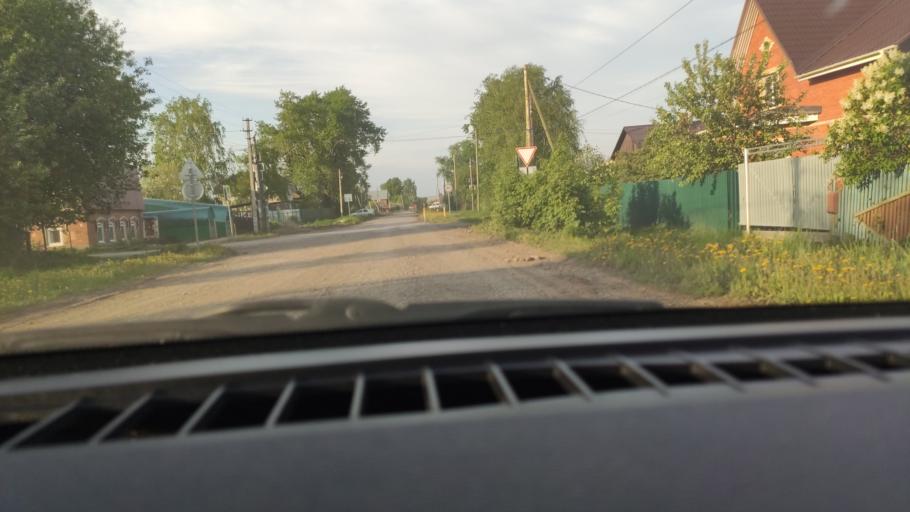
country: RU
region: Perm
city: Kultayevo
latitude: 57.9318
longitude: 56.0174
